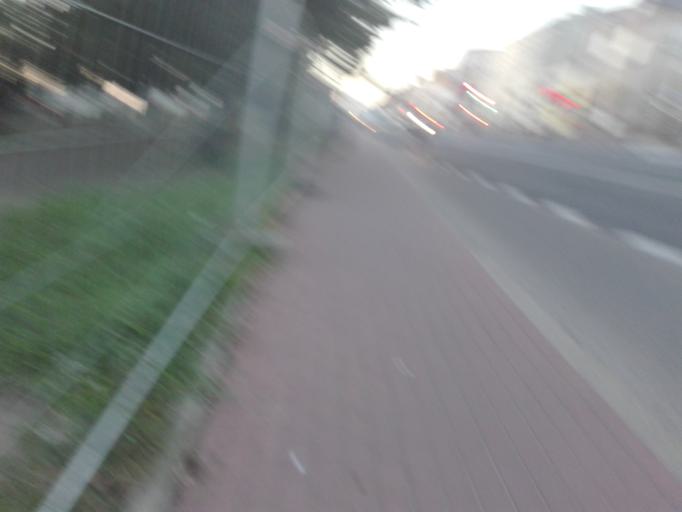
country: PL
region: Masovian Voivodeship
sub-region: Powiat sochaczewski
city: Sochaczew
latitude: 52.2285
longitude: 20.2383
